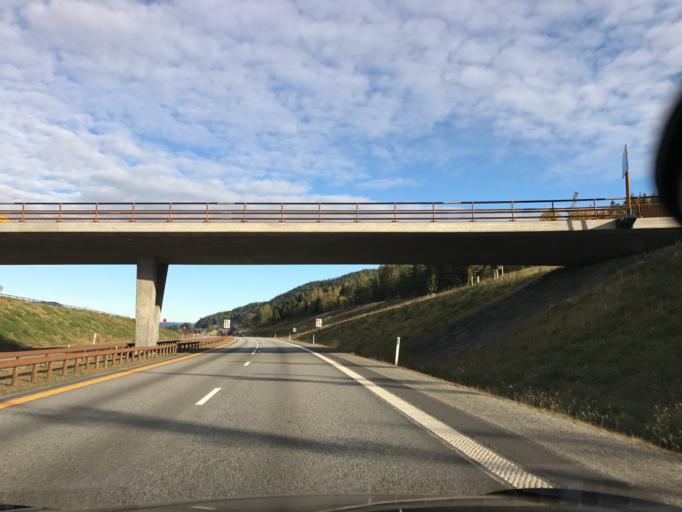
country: NO
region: Akershus
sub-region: Eidsvoll
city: Eidsvoll
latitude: 60.4133
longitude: 11.2412
